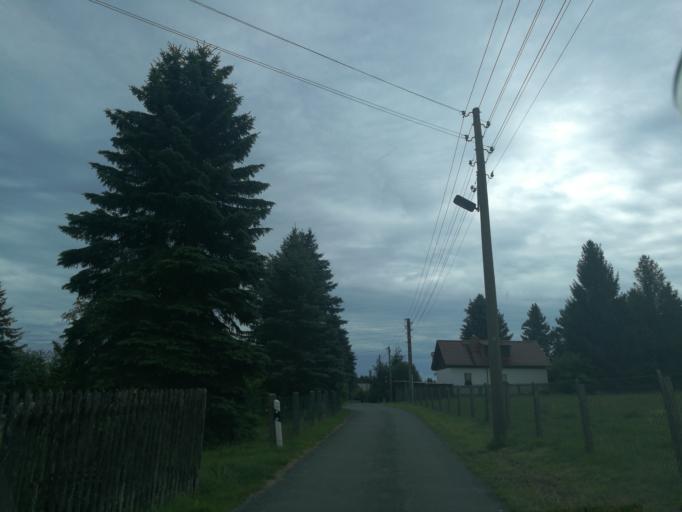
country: DE
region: Saxony
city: Adorf
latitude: 50.3083
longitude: 12.2780
